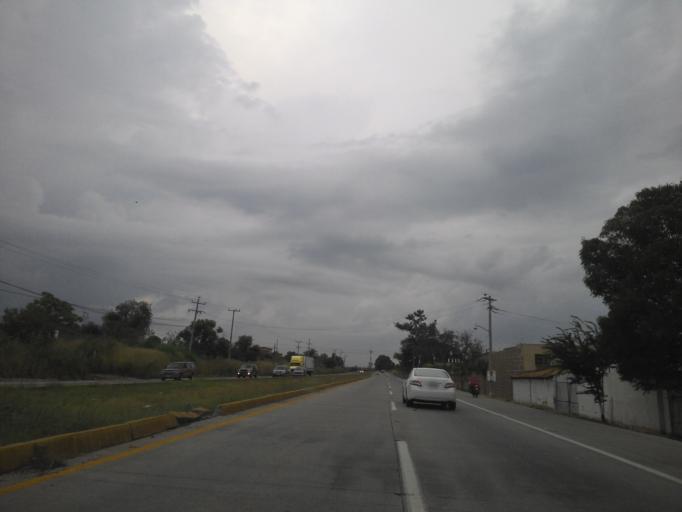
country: MX
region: Jalisco
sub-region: Zapotlanejo
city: La Mezquitera
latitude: 20.5974
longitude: -103.1042
